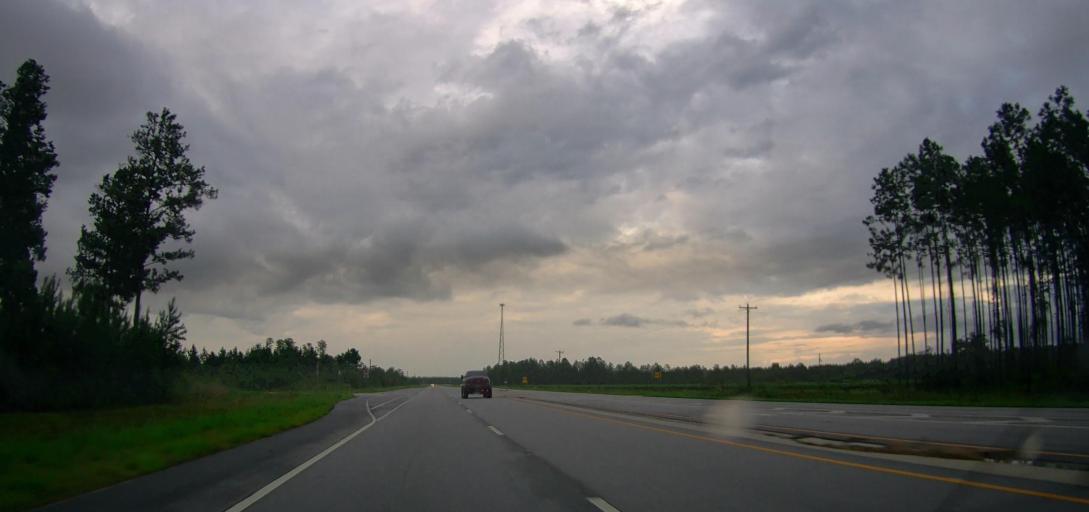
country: US
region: Georgia
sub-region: Ware County
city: Deenwood
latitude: 31.1374
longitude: -82.4924
